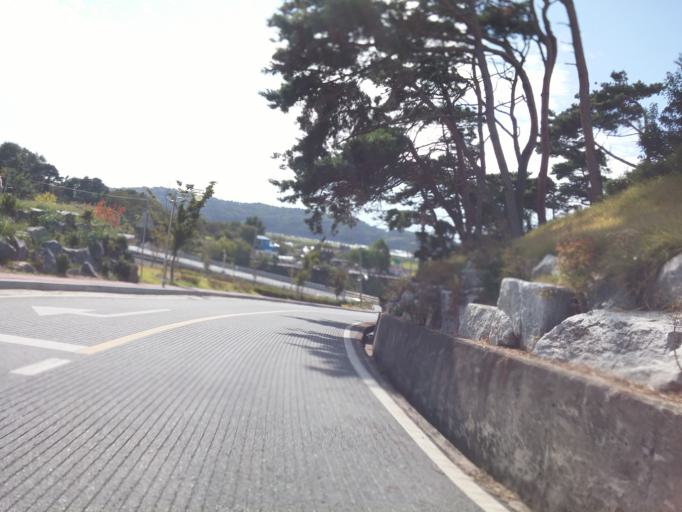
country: KR
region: Chungcheongnam-do
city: Yonmu
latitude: 36.1760
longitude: 127.1489
